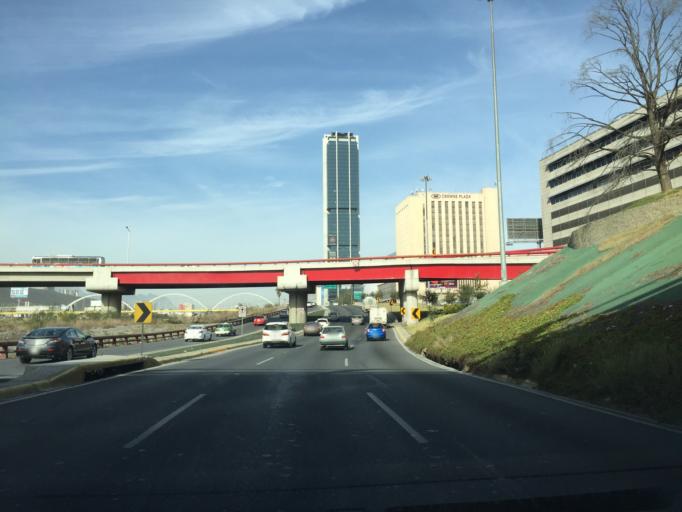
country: MX
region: Nuevo Leon
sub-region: Monterrey
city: Monterrey
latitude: 25.6634
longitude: -100.3112
